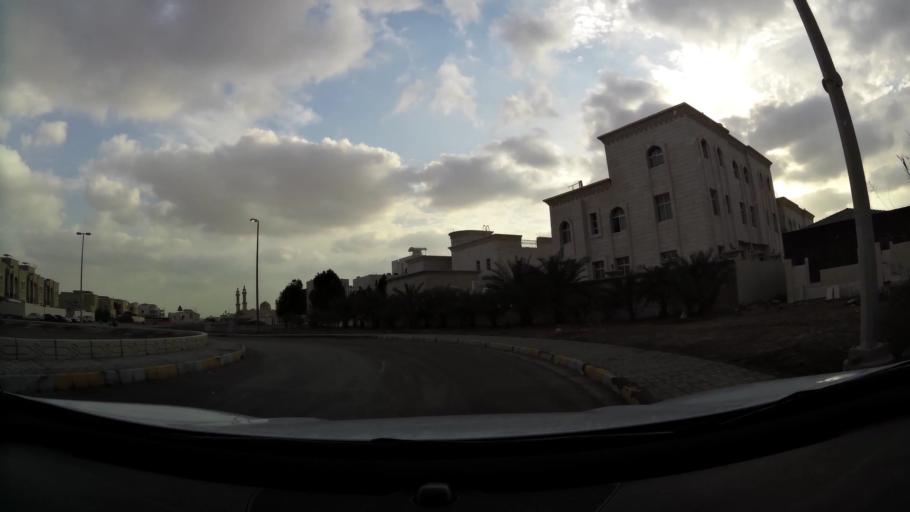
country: AE
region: Abu Dhabi
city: Abu Dhabi
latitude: 24.3567
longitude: 54.5585
